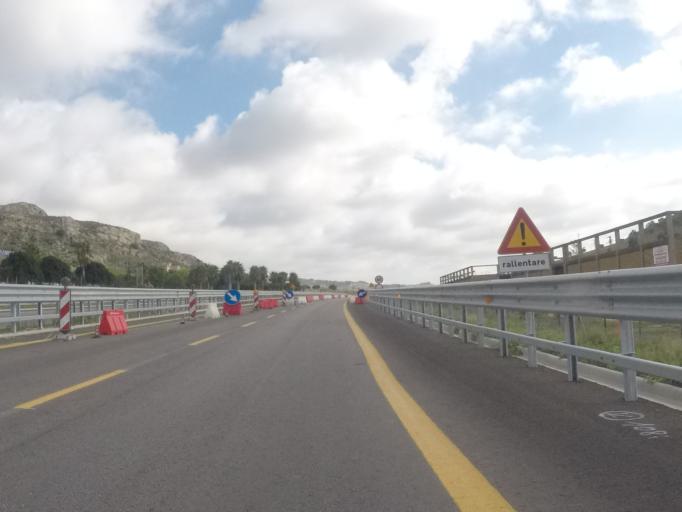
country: IT
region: Sicily
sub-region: Provincia di Caltanissetta
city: San Cataldo
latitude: 37.4450
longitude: 13.9534
